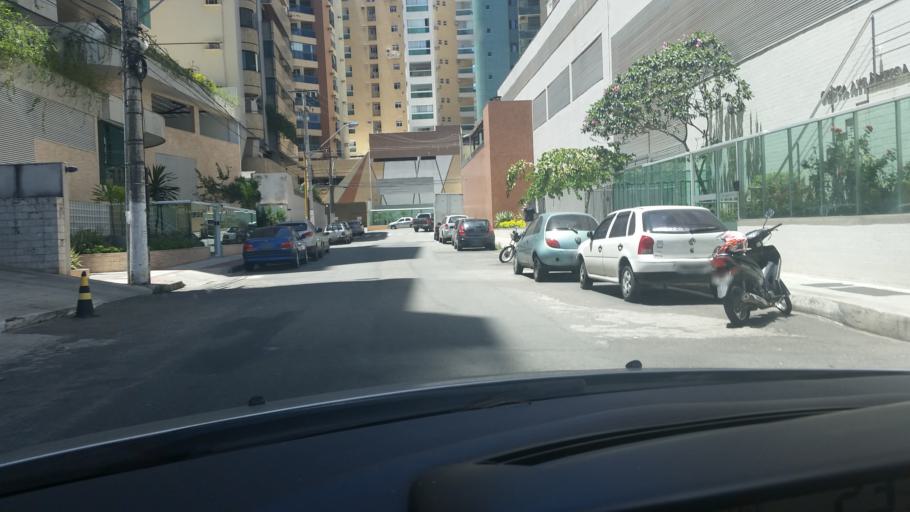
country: BR
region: Espirito Santo
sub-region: Vila Velha
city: Vila Velha
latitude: -20.3332
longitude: -40.2822
